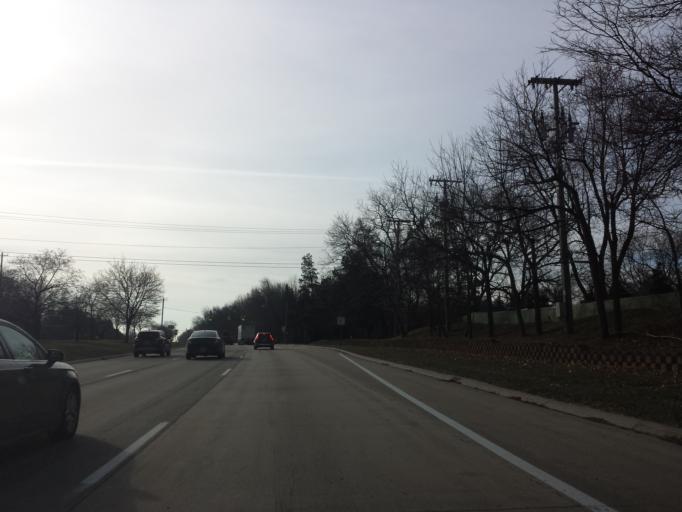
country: US
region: Michigan
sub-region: Oakland County
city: Franklin
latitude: 42.5600
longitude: -83.2855
